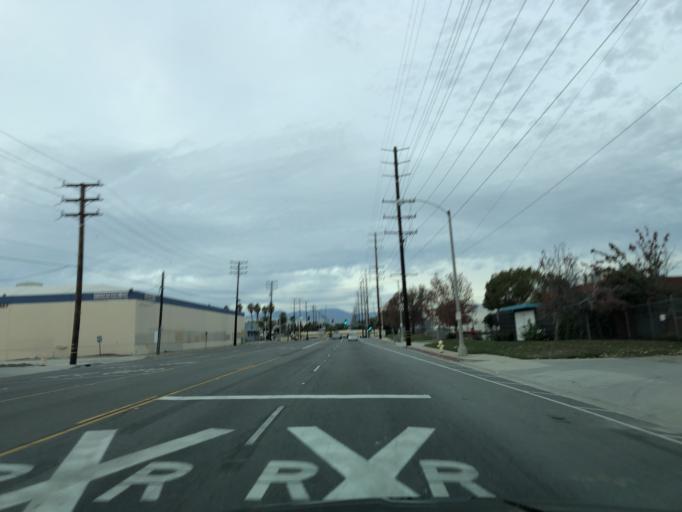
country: US
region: California
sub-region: Los Angeles County
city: Norwalk
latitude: 33.9046
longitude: -118.0467
